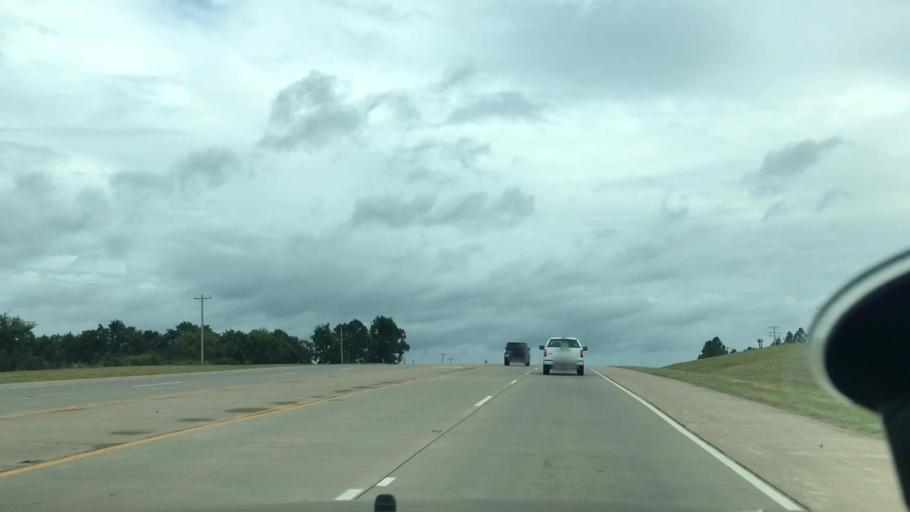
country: US
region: Oklahoma
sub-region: Seminole County
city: Seminole
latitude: 35.2736
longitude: -96.6706
